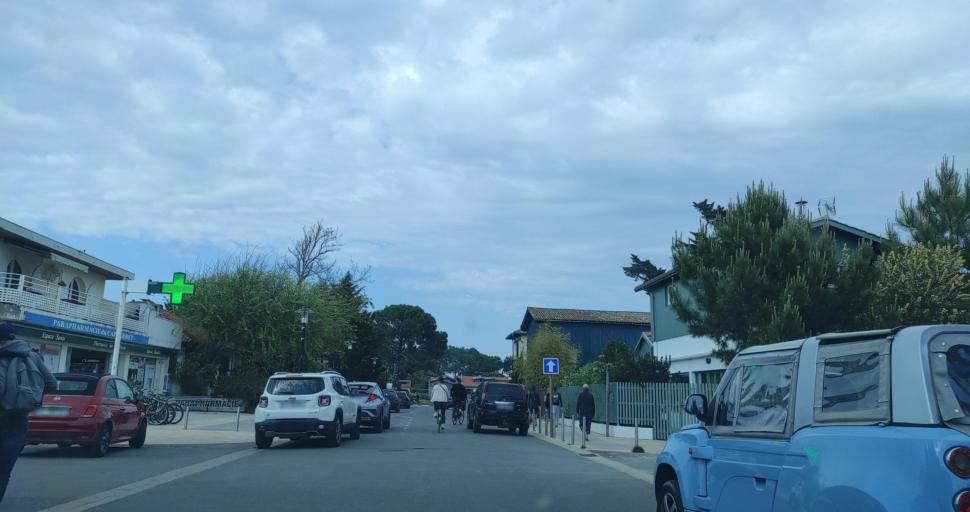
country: FR
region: Aquitaine
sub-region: Departement de la Gironde
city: Arcachon
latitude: 44.6547
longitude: -1.2409
